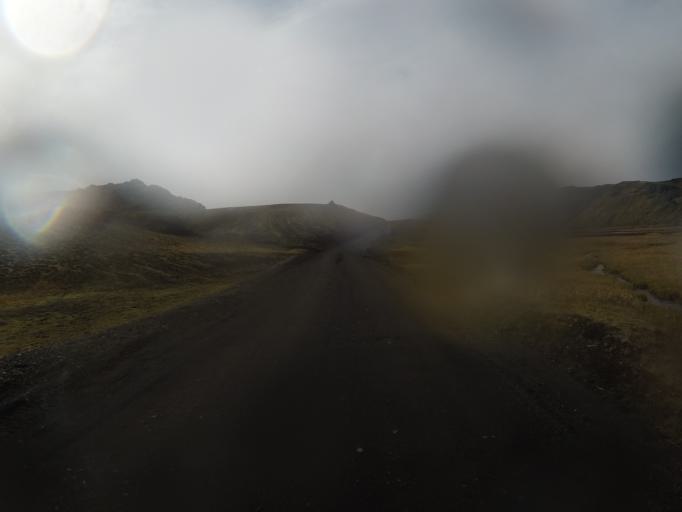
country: IS
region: South
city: Vestmannaeyjar
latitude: 63.9813
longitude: -18.8641
